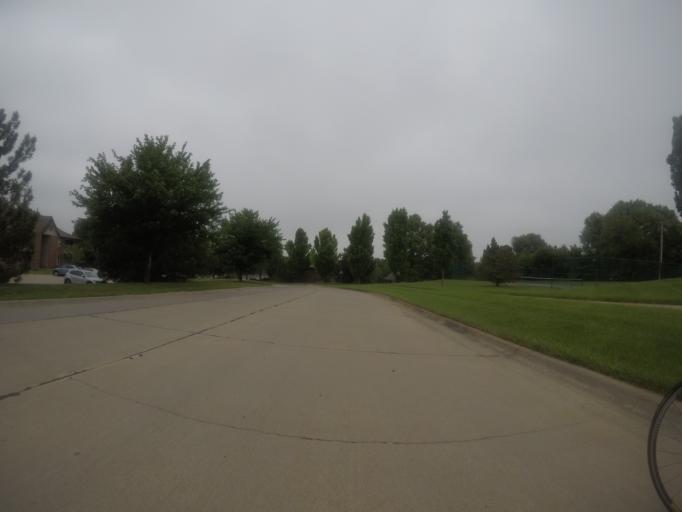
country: US
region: Kansas
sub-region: Riley County
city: Manhattan
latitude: 39.1940
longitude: -96.6035
